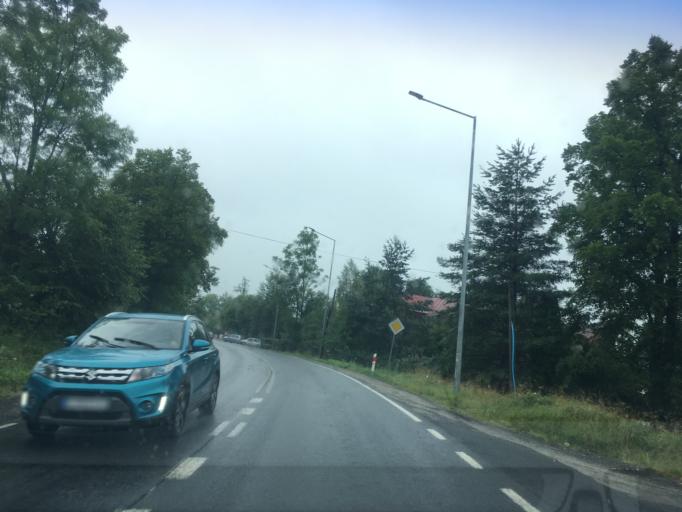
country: PL
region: Lesser Poland Voivodeship
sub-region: Powiat tatrzanski
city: Koscielisko
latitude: 49.2765
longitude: 19.8871
